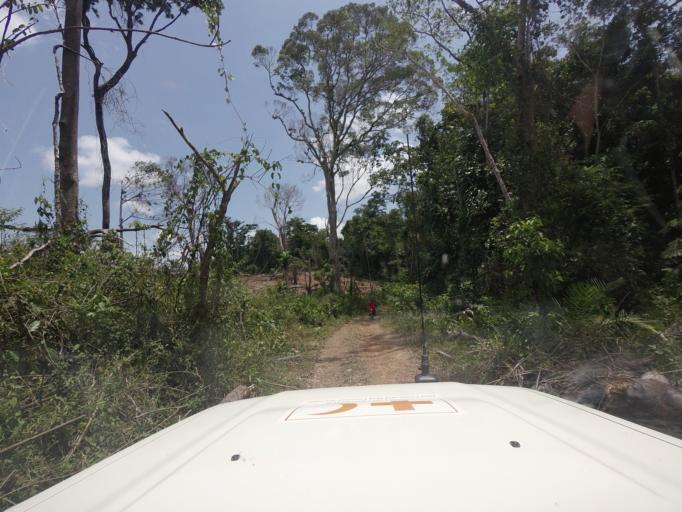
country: GN
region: Nzerekore
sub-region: Yomou
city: Yomou
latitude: 7.3758
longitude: -9.3103
